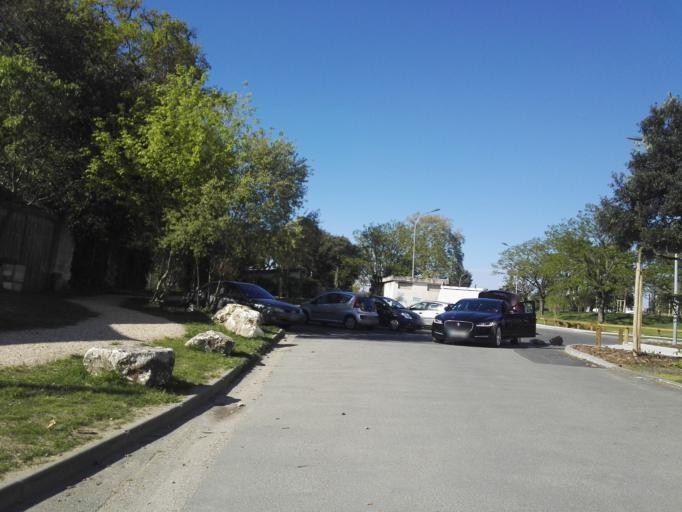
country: FR
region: Aquitaine
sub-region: Departement de la Gironde
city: Talence
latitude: 44.7928
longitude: -0.5872
